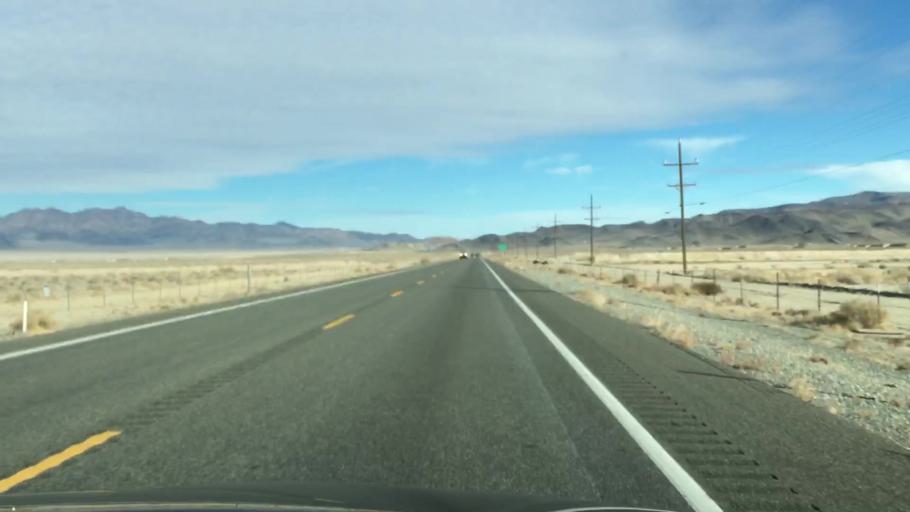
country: US
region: Nevada
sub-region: Mineral County
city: Hawthorne
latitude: 38.5268
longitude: -118.5653
